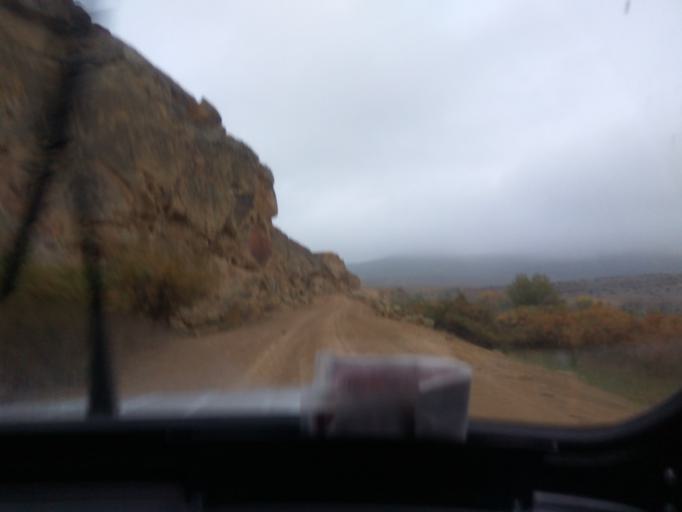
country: RU
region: Dagestan
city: Korkmaskala
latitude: 42.9854
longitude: 47.1890
